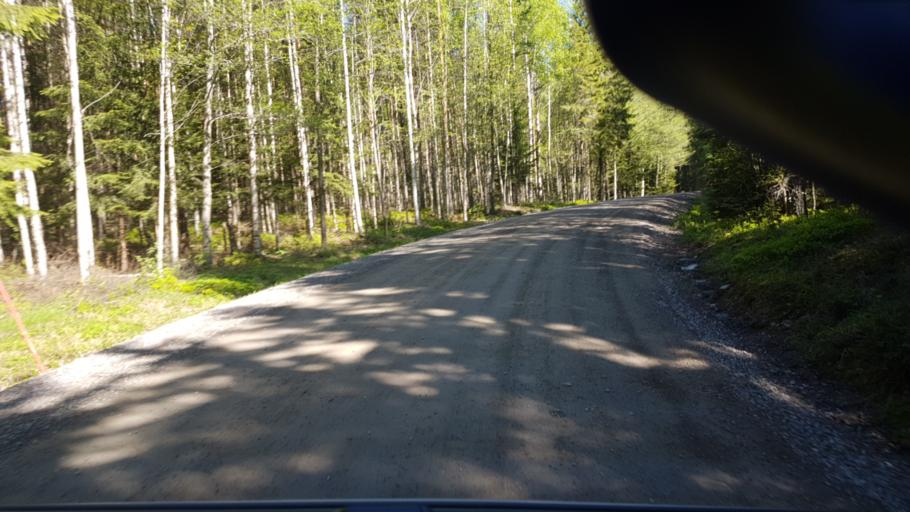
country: SE
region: Vaermland
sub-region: Arvika Kommun
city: Arvika
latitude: 59.8289
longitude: 12.6028
